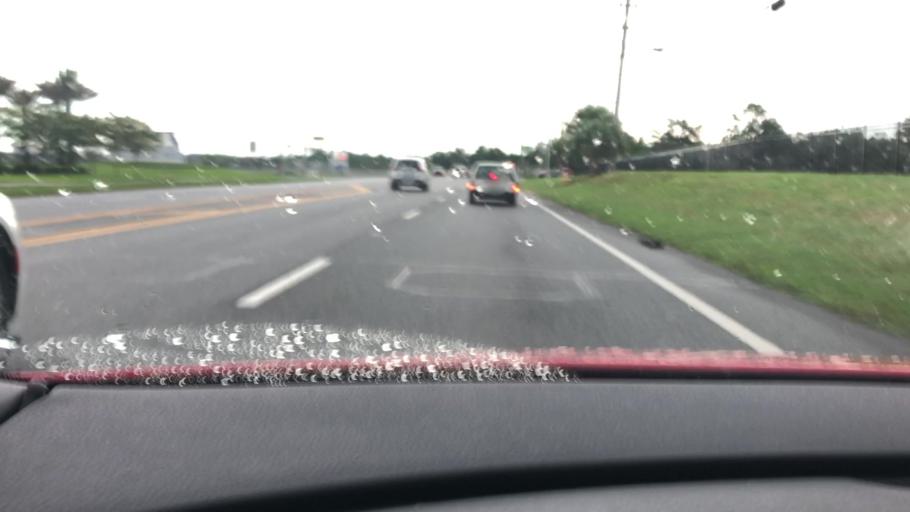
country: US
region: Florida
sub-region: Volusia County
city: Daytona Beach
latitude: 29.1835
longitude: -81.0422
